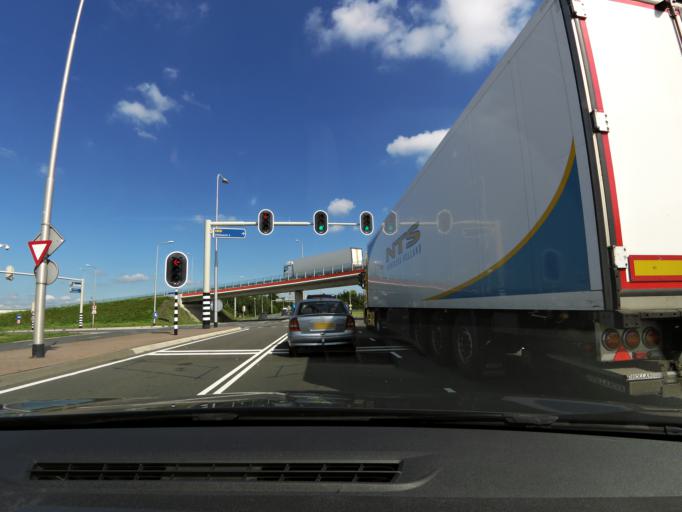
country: NL
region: North Holland
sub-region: Gemeente Aalsmeer
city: Aalsmeer
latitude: 52.2612
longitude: 4.7954
